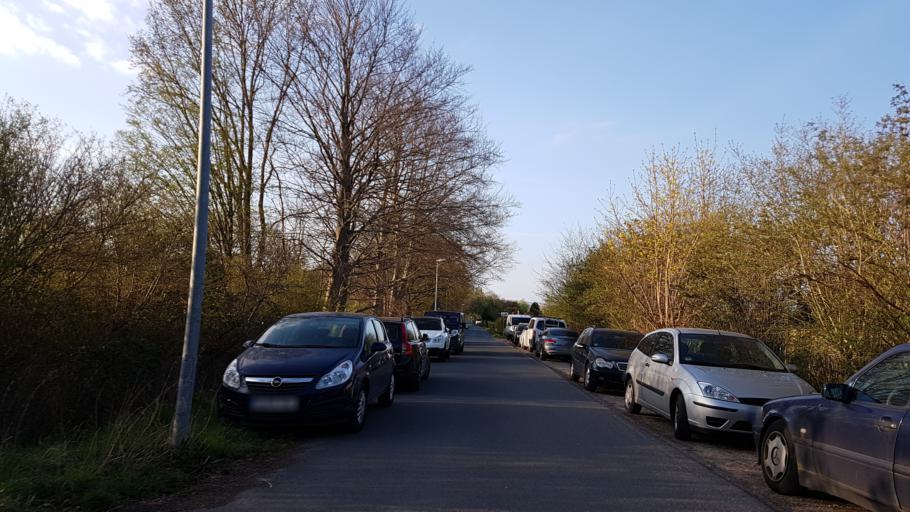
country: DE
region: Lower Saxony
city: Ronnenberg
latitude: 52.3547
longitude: 9.6876
